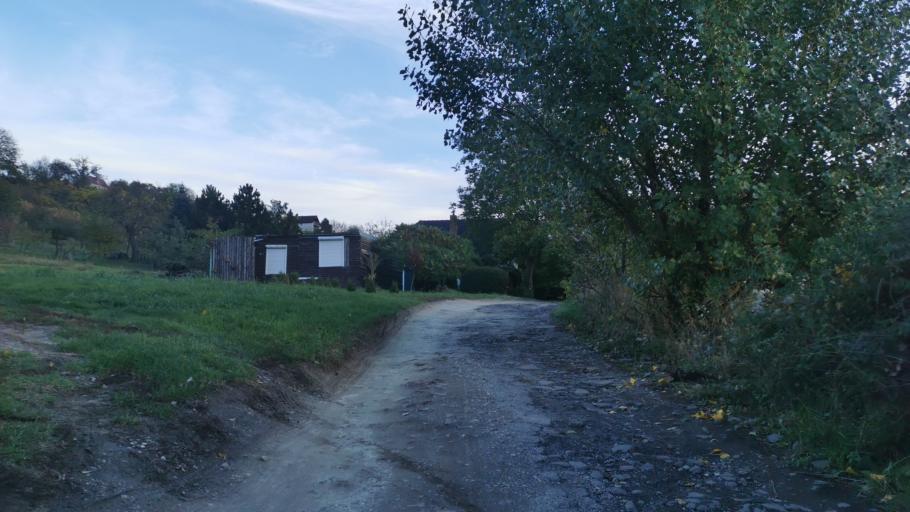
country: SK
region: Trnavsky
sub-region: Okres Skalica
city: Skalica
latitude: 48.8238
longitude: 17.2302
